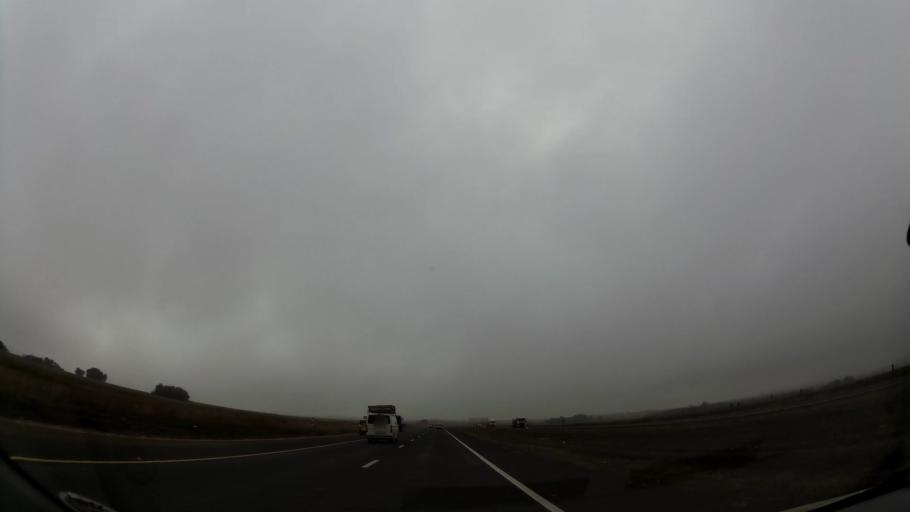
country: ZA
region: Mpumalanga
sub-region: Nkangala District Municipality
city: Delmas
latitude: -26.0737
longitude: 28.7383
